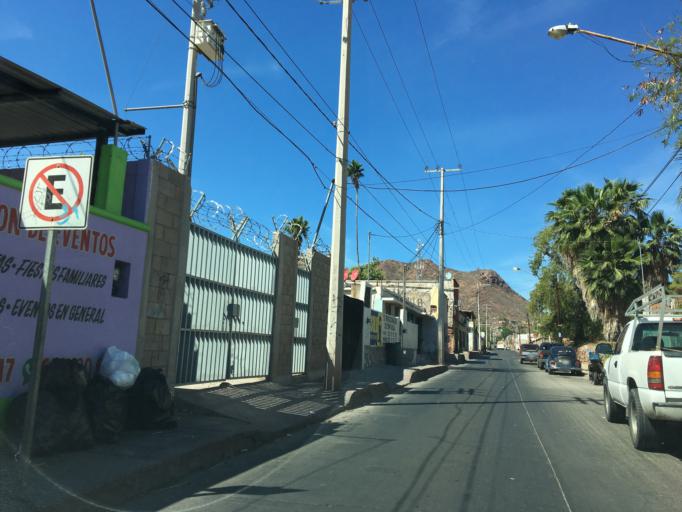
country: MX
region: Sonora
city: Heroica Guaymas
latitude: 27.9225
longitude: -110.8968
